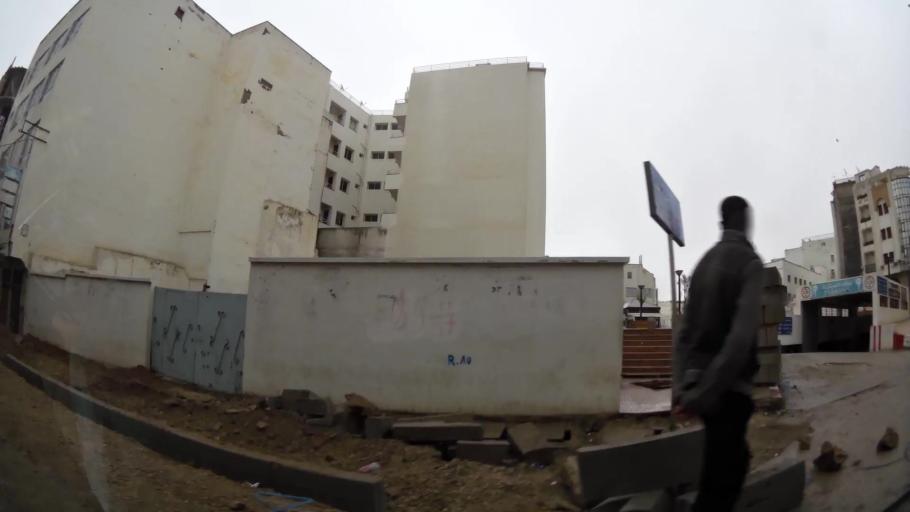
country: MA
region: Taza-Al Hoceima-Taounate
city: Al Hoceima
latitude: 35.2418
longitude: -3.9301
